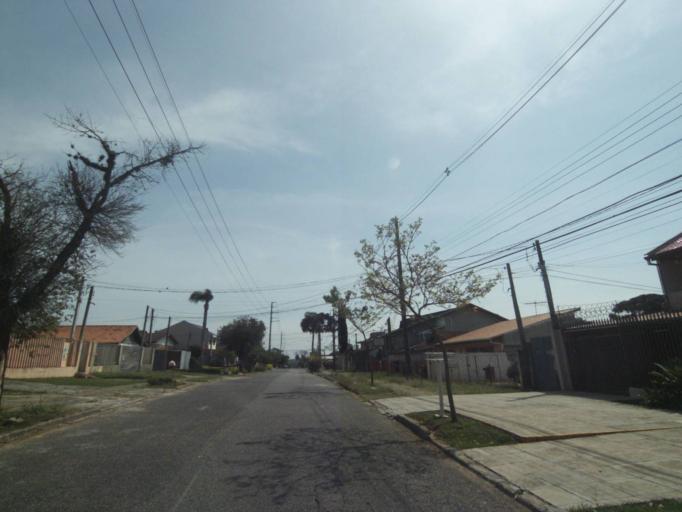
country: BR
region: Parana
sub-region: Curitiba
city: Curitiba
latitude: -25.4634
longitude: -49.3027
